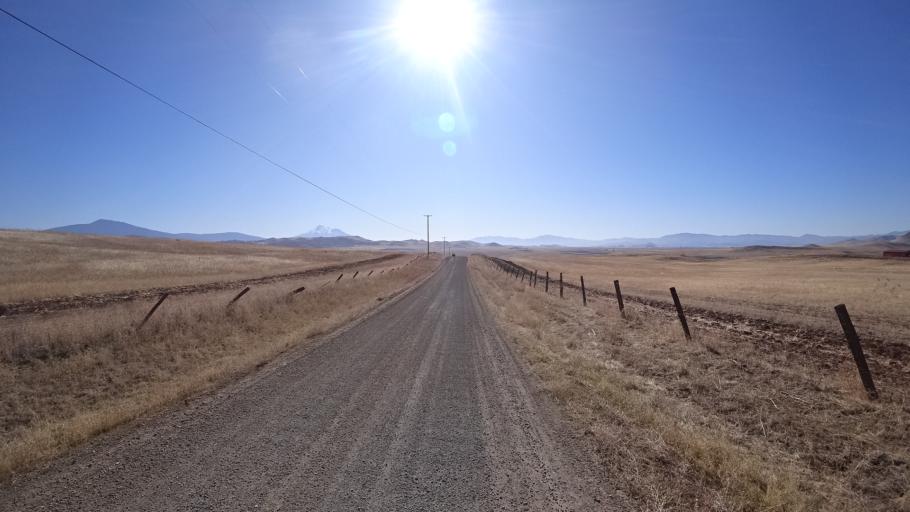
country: US
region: California
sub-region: Siskiyou County
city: Montague
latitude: 41.8428
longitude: -122.4206
